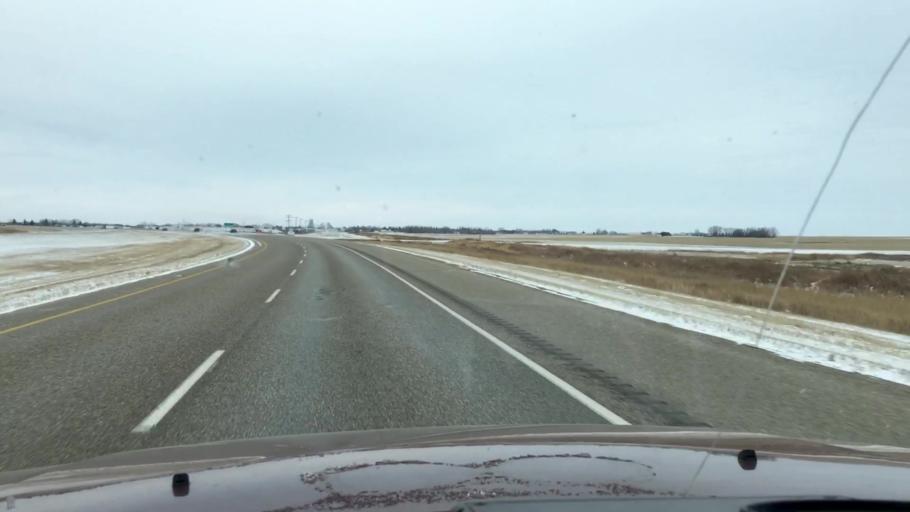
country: CA
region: Saskatchewan
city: Watrous
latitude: 51.0686
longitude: -105.8380
